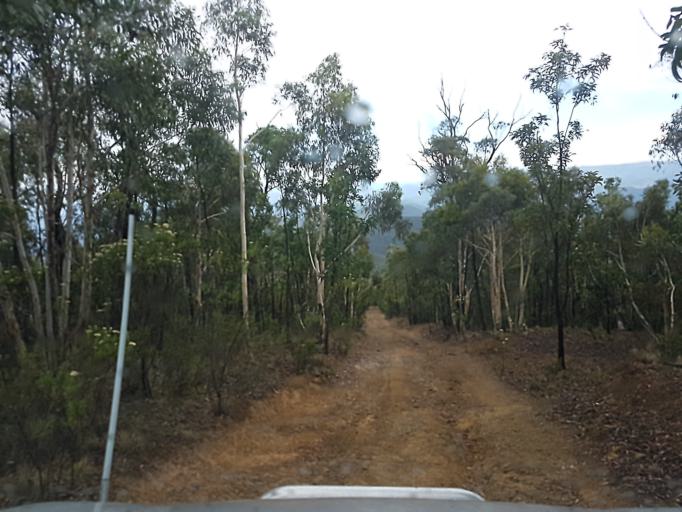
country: AU
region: New South Wales
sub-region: Snowy River
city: Jindabyne
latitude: -36.9127
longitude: 148.3354
